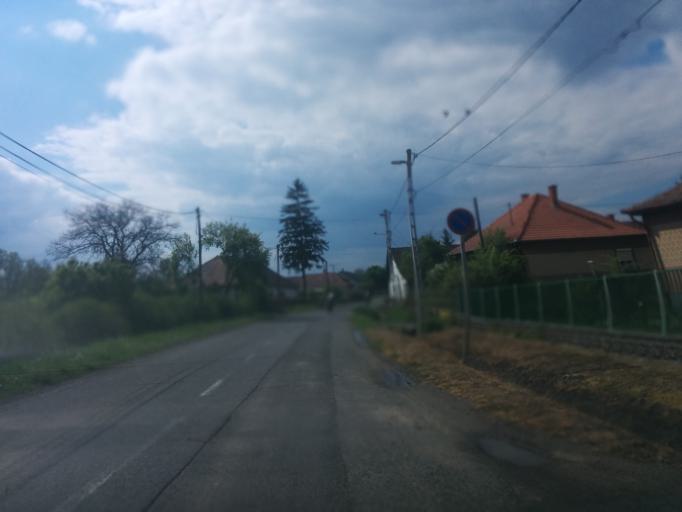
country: HU
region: Nograd
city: Bercel
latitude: 47.8666
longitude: 19.4087
